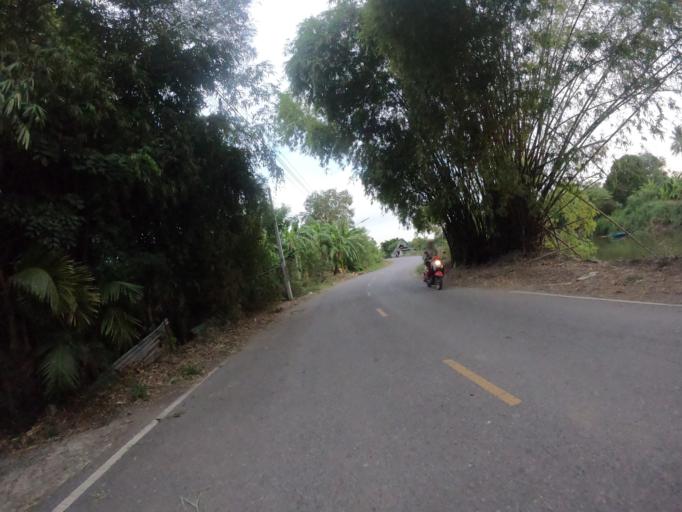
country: TH
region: Pathum Thani
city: Ban Lam Luk Ka
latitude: 14.0028
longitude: 100.7983
